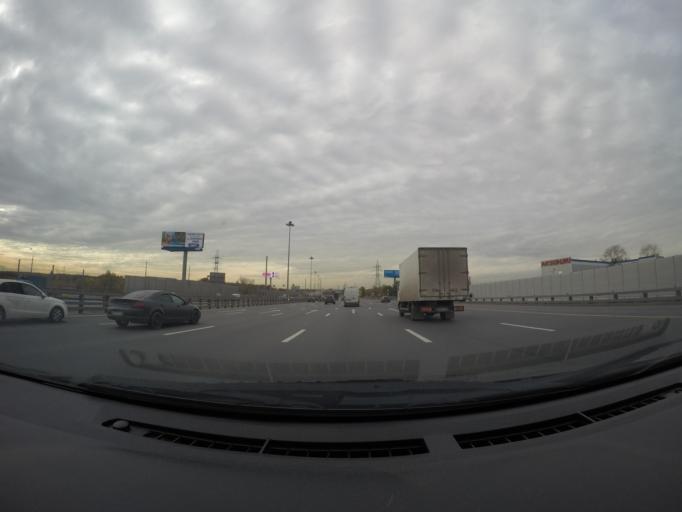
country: RU
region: Moskovskaya
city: Druzhba
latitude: 55.9088
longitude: 37.7706
